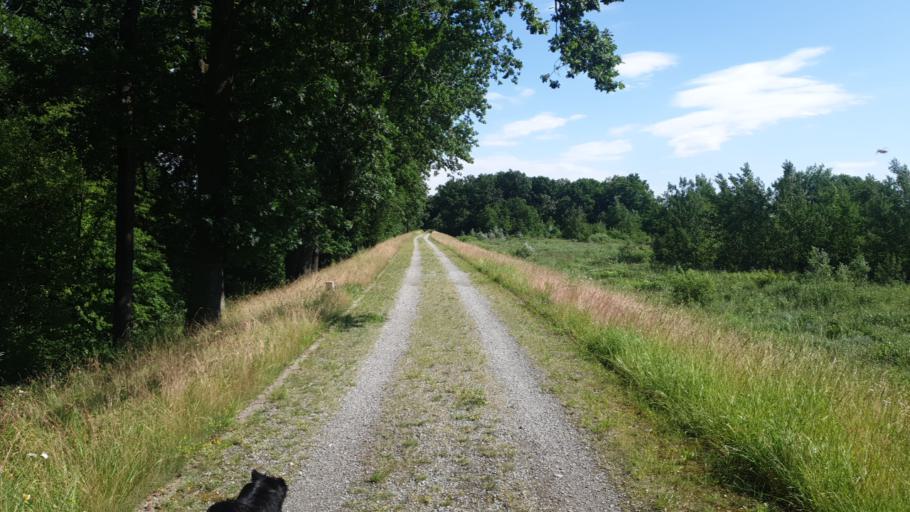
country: PL
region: Lower Silesian Voivodeship
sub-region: Powiat wroclawski
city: Radwanice
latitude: 51.0883
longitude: 17.1163
